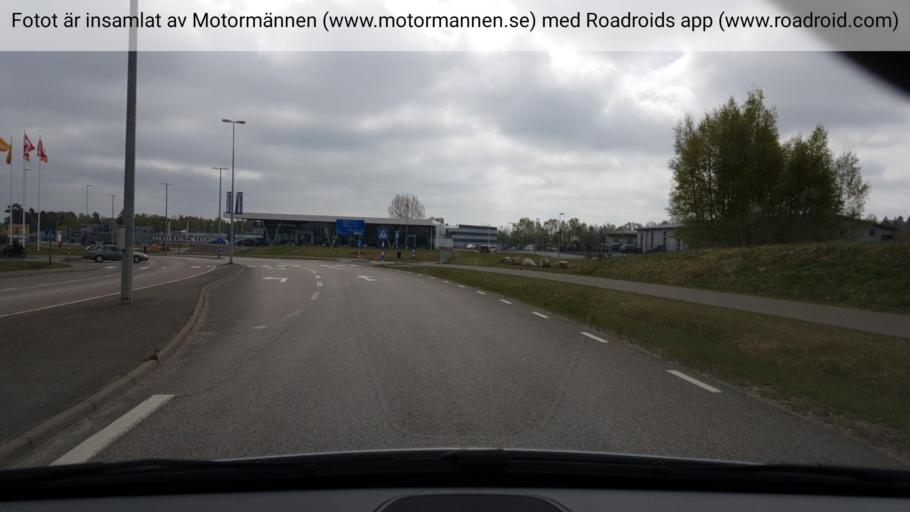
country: SE
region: Vaestra Goetaland
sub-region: Skovde Kommun
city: Skoevde
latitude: 58.4202
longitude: 13.8645
